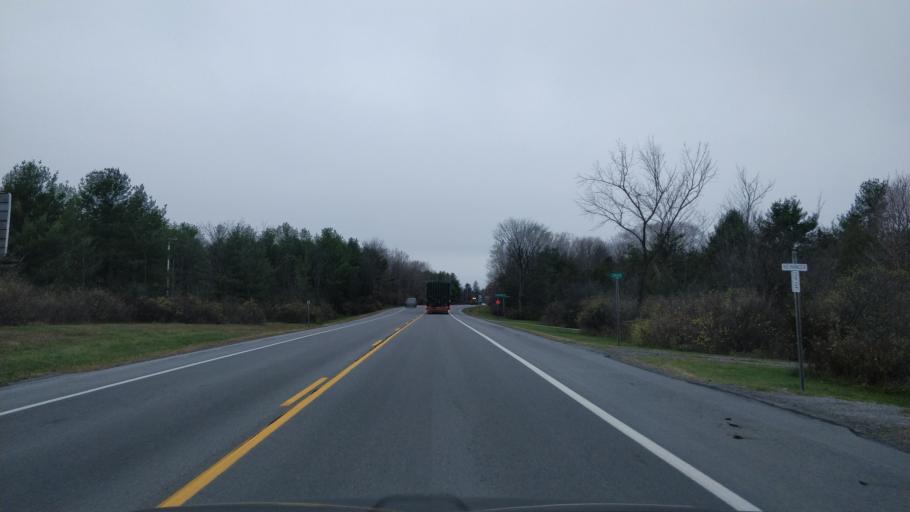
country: CA
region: Ontario
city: Brockville
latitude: 44.6052
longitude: -75.6178
